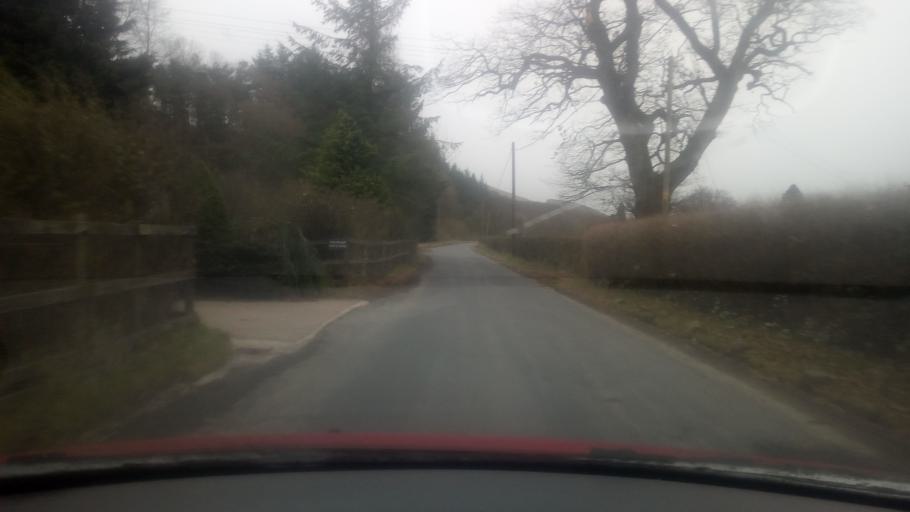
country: GB
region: Scotland
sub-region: The Scottish Borders
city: Jedburgh
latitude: 55.3901
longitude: -2.6541
